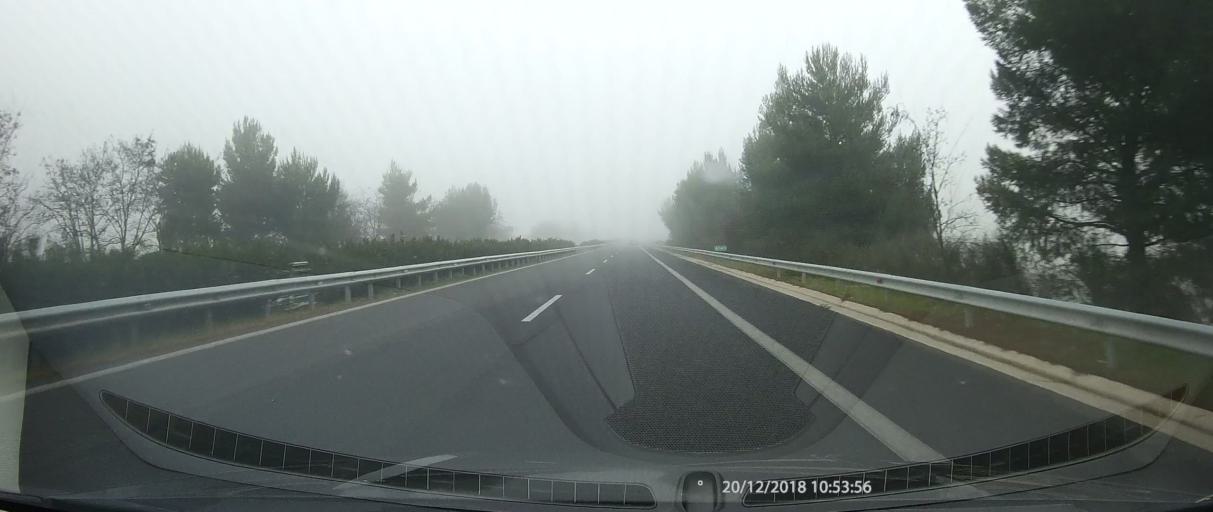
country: GR
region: Peloponnese
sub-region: Nomos Arkadias
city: Tripoli
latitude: 37.6181
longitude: 22.4591
